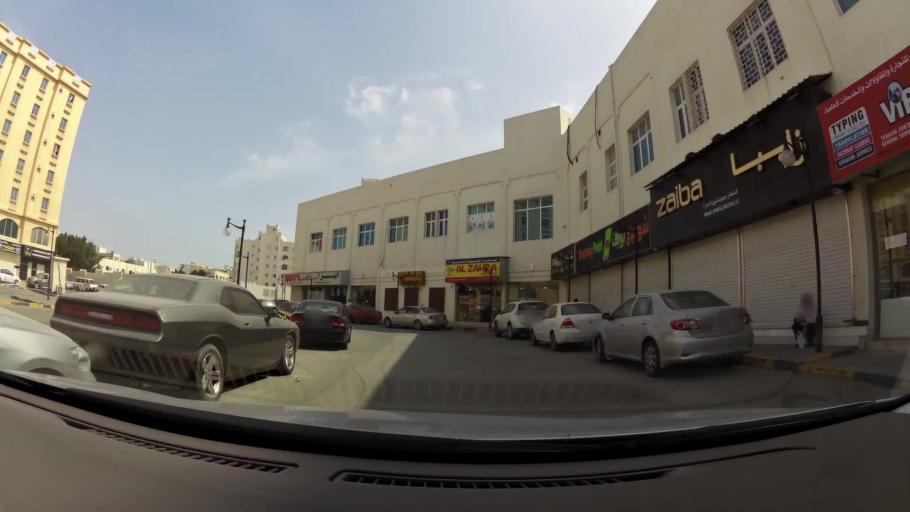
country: QA
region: Baladiyat ad Dawhah
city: Doha
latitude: 25.2795
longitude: 51.5364
